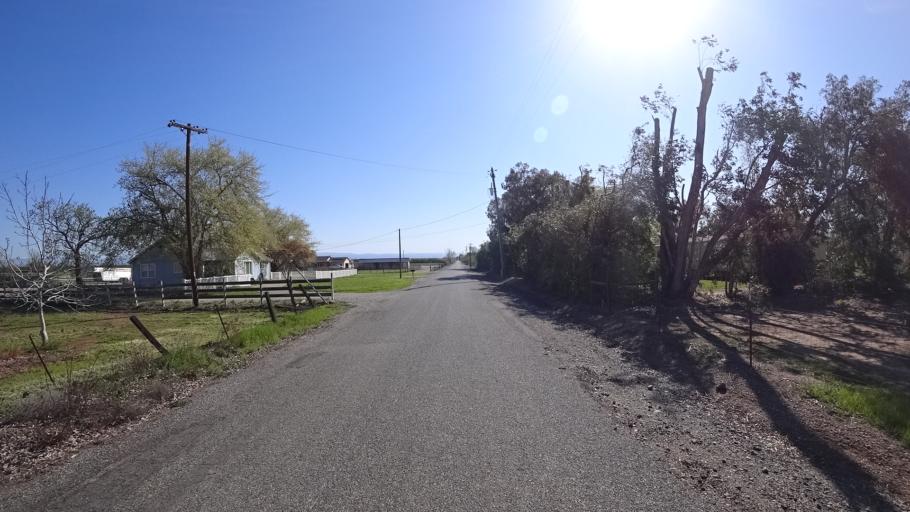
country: US
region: California
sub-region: Glenn County
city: Hamilton City
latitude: 39.7825
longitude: -122.0997
